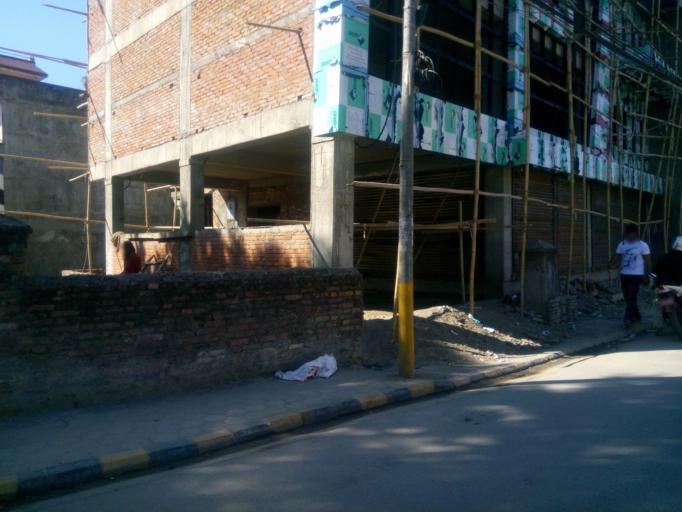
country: NP
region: Central Region
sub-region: Bagmati Zone
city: Kathmandu
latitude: 27.7222
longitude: 85.3313
